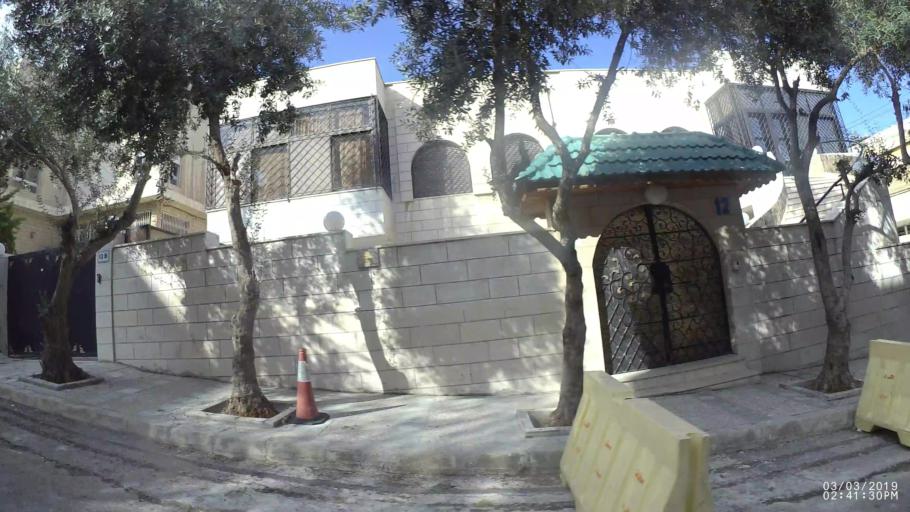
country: JO
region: Amman
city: Amman
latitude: 31.9620
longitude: 35.8933
